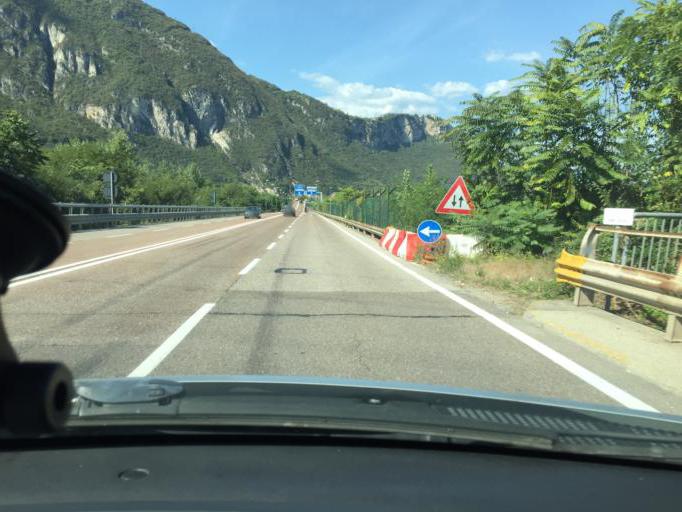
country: IT
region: Trentino-Alto Adige
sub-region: Provincia di Trento
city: Ravina
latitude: 46.0437
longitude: 11.1180
